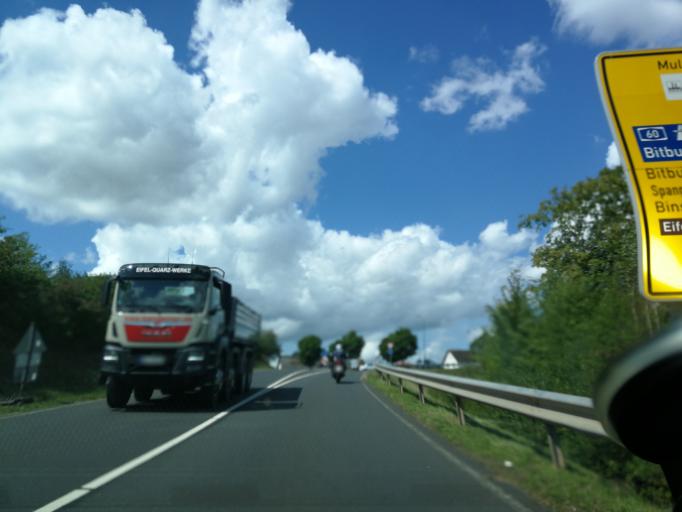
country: DE
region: Rheinland-Pfalz
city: Binsfeld
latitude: 49.9654
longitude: 6.7133
